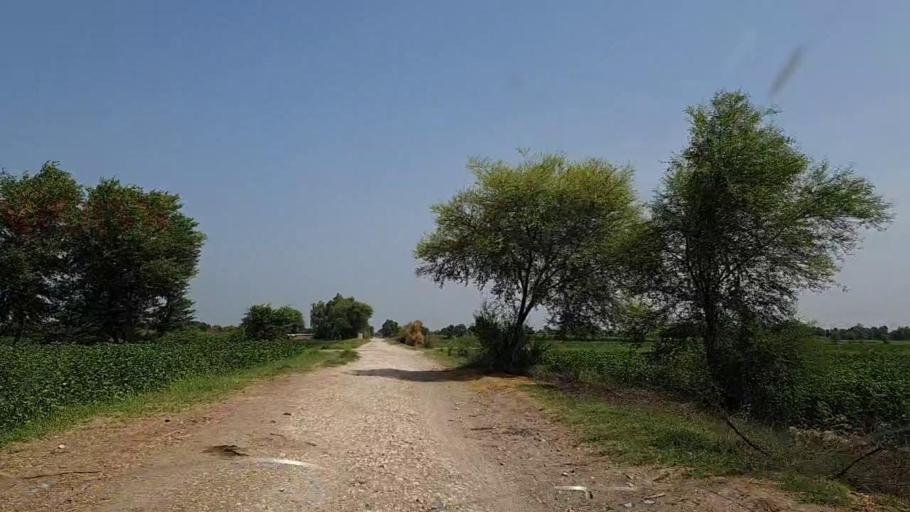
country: PK
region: Sindh
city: Adilpur
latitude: 27.8359
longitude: 69.2834
